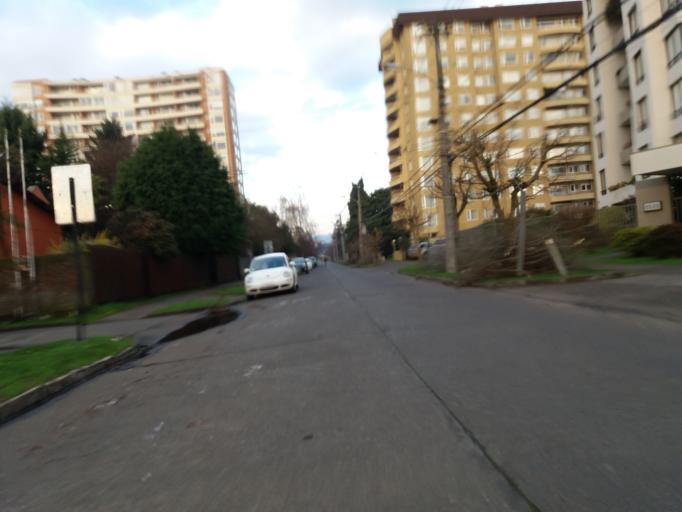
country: CL
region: Araucania
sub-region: Provincia de Cautin
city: Temuco
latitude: -38.7381
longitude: -72.6101
